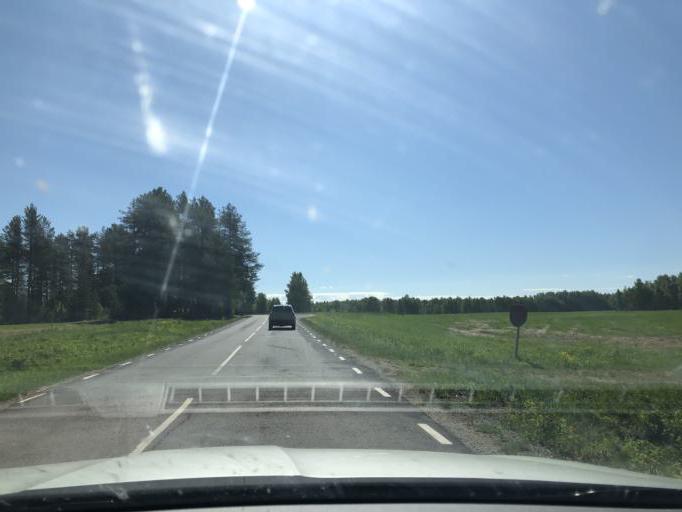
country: SE
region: Norrbotten
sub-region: Lulea Kommun
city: Gammelstad
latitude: 65.6587
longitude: 21.9943
